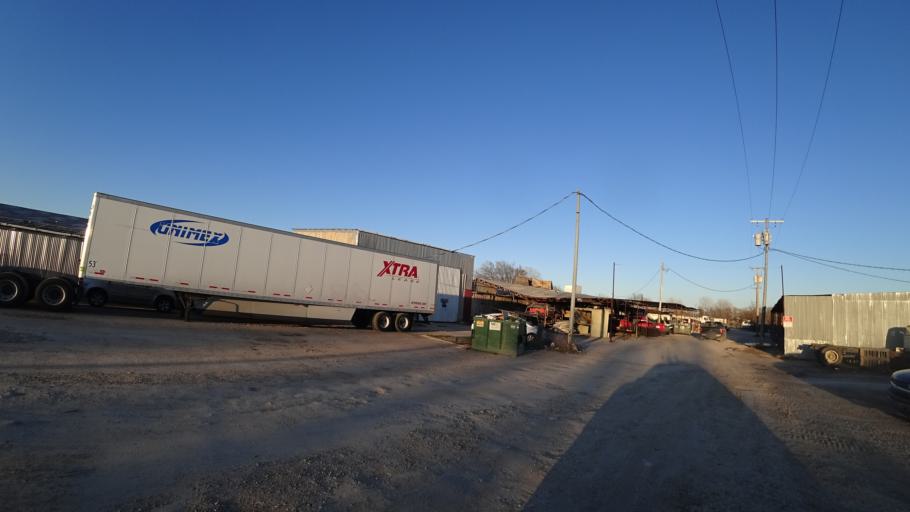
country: US
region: Texas
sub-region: Denton County
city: Lewisville
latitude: 33.0305
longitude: -96.9900
